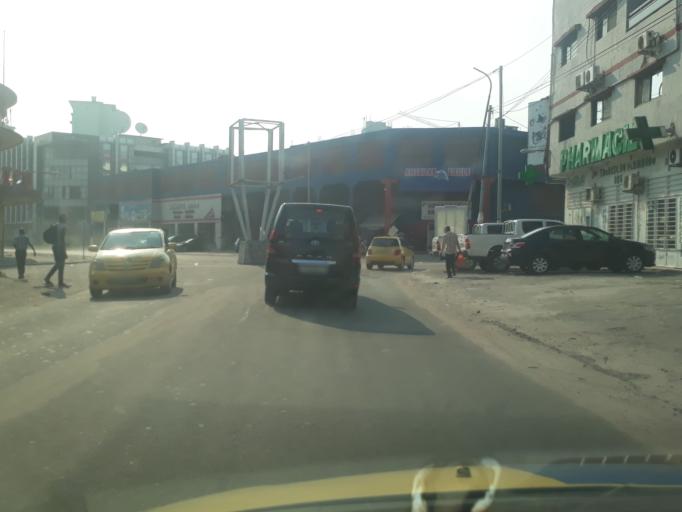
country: CD
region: Kinshasa
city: Kinshasa
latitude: -4.3043
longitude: 15.3188
